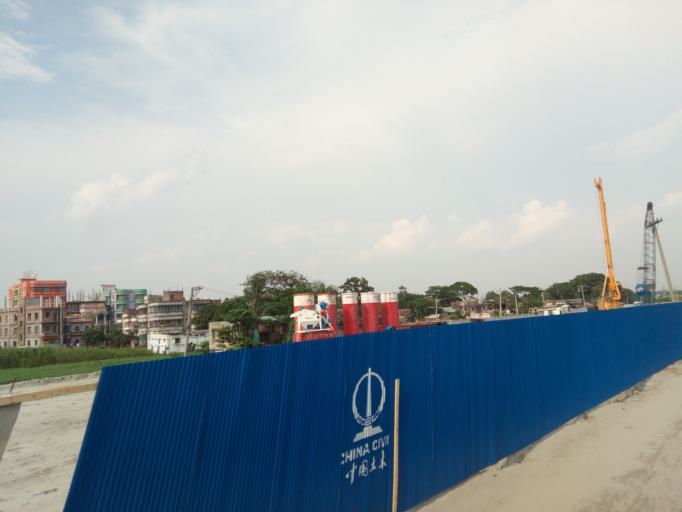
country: BD
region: Dhaka
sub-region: Dhaka
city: Dhaka
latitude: 23.6604
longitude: 90.3617
